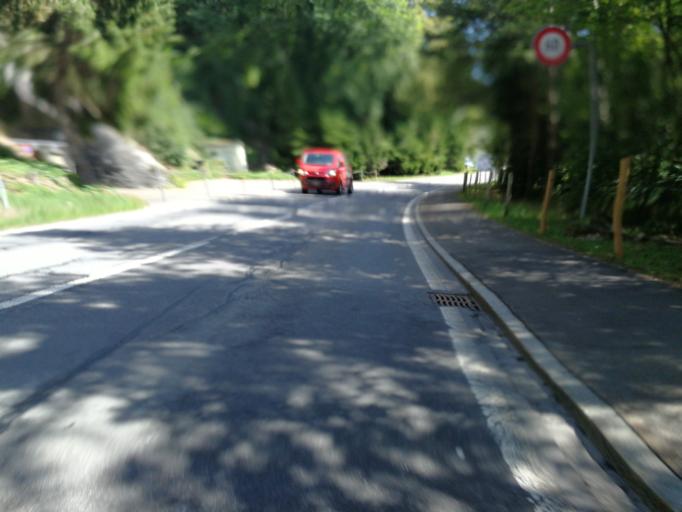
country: CH
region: Schwyz
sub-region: Bezirk Schwyz
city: Ingenbohl
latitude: 46.9997
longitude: 8.5746
